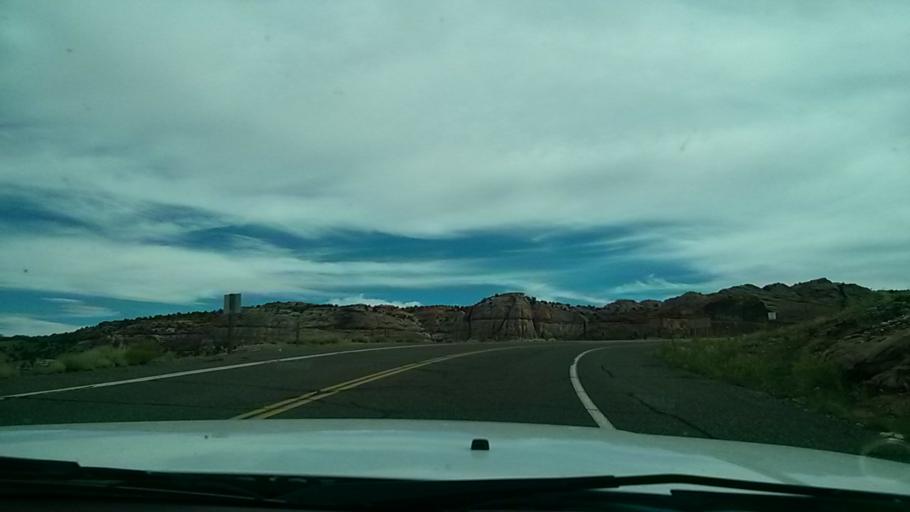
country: US
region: Utah
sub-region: Wayne County
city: Loa
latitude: 37.7740
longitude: -111.4152
